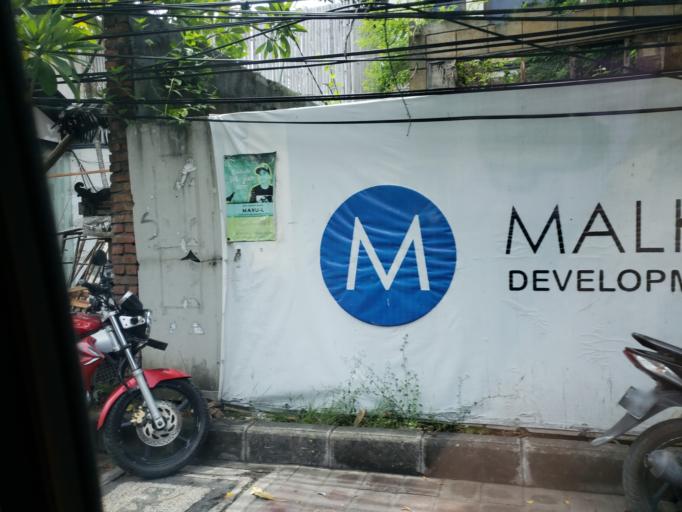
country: ID
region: Bali
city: Kuta
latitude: -8.6798
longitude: 115.1535
